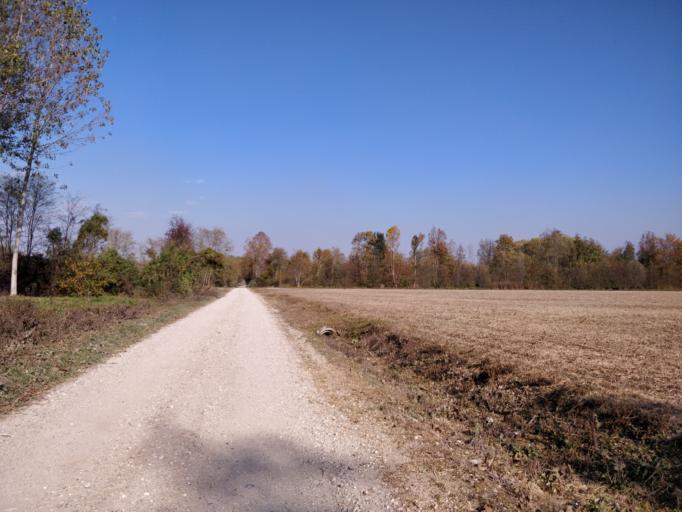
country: IT
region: Friuli Venezia Giulia
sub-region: Provincia di Udine
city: Bertiolo
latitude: 45.9279
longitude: 13.0377
